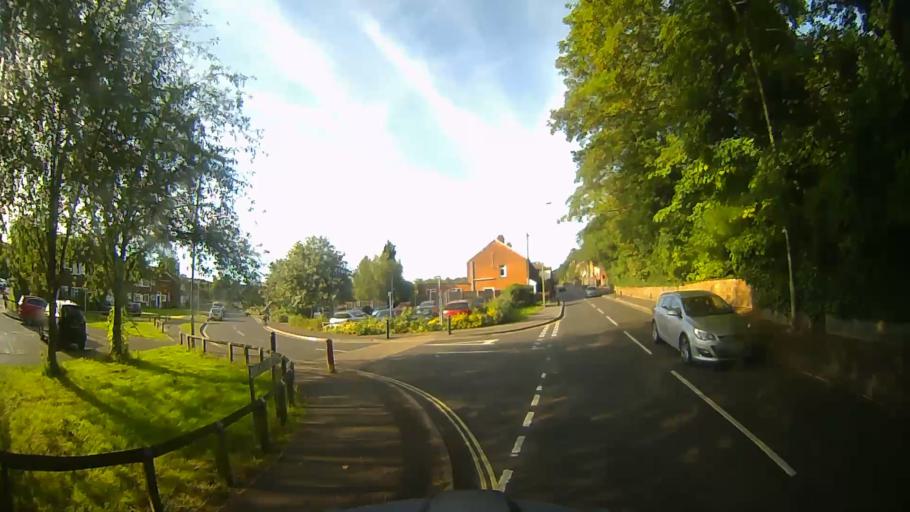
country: GB
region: England
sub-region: Hampshire
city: Basingstoke
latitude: 51.2599
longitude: -1.0953
